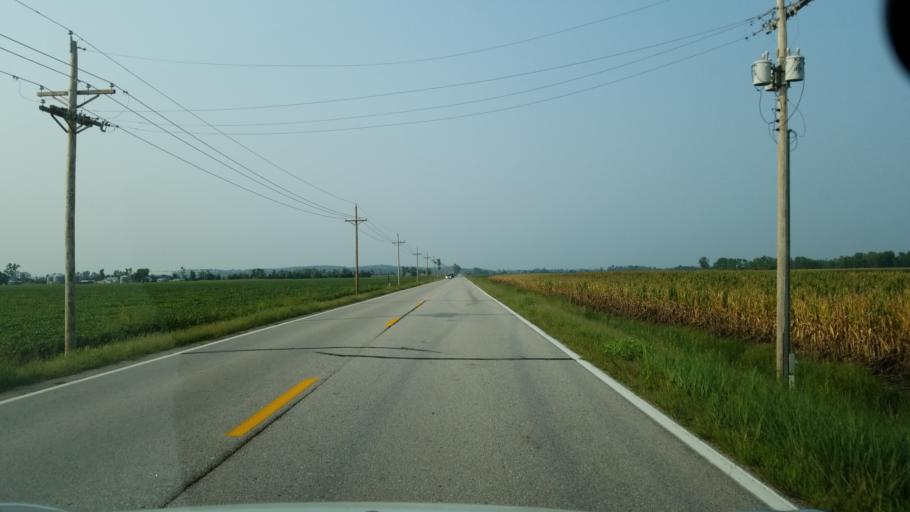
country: US
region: Nebraska
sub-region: Sarpy County
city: Offutt Air Force Base
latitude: 41.0893
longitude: -95.8898
